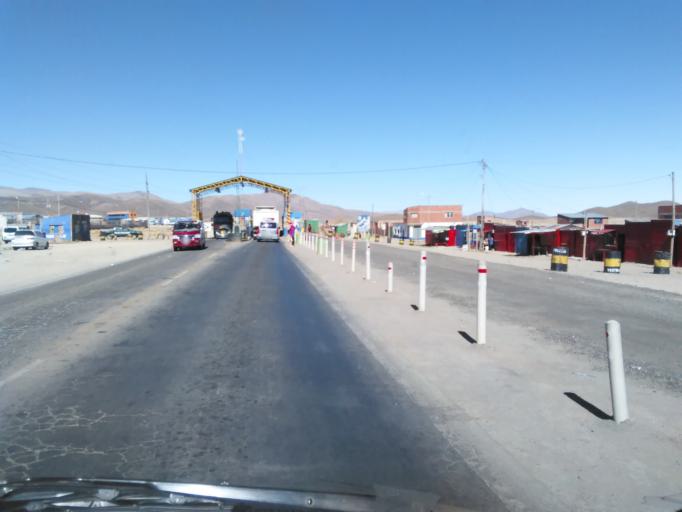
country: BO
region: Oruro
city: Oruro
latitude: -18.0178
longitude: -67.0315
